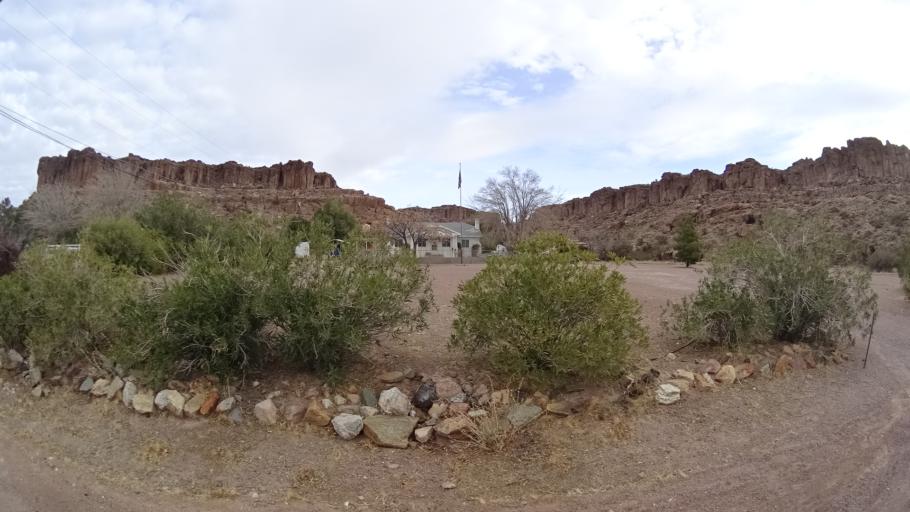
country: US
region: Arizona
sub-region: Mohave County
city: Kingman
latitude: 35.2021
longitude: -114.0751
